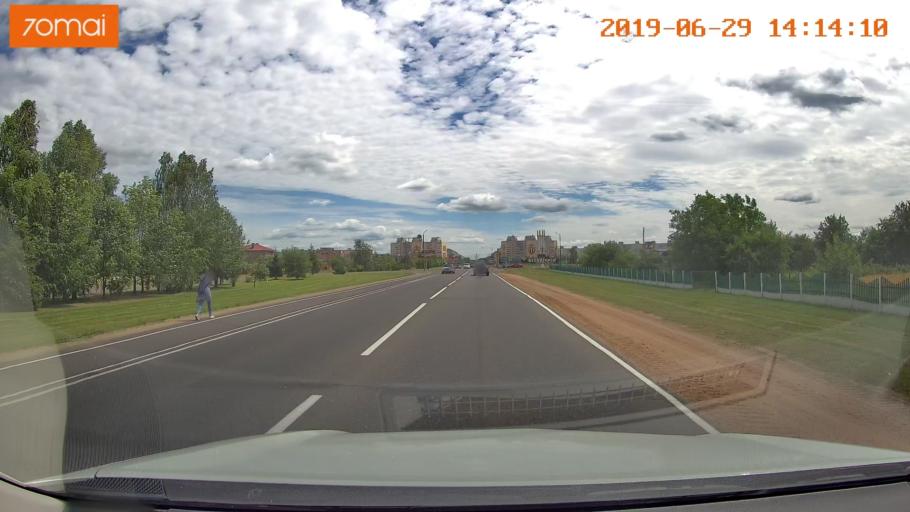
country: BY
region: Minsk
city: Salihorsk
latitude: 52.7972
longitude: 27.5150
